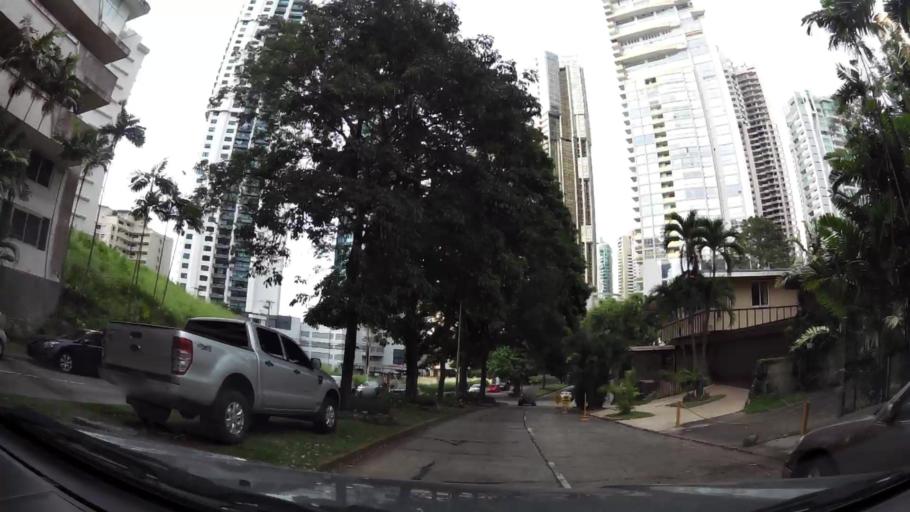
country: PA
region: Panama
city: Panama
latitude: 8.9742
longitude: -79.5136
